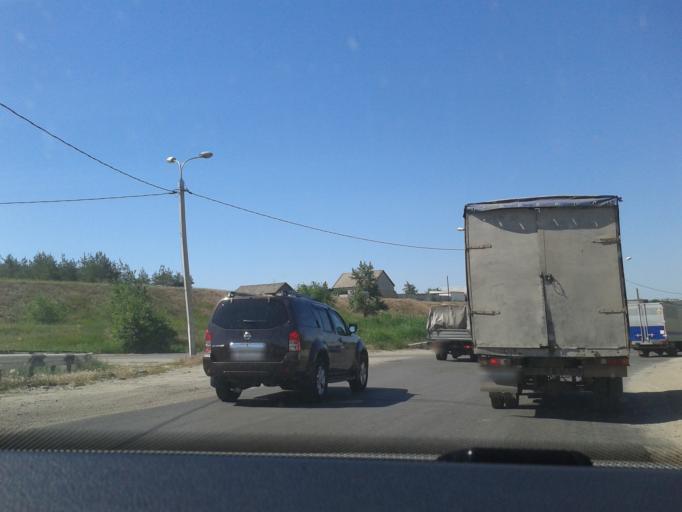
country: RU
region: Volgograd
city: Volgograd
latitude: 48.7062
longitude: 44.4413
